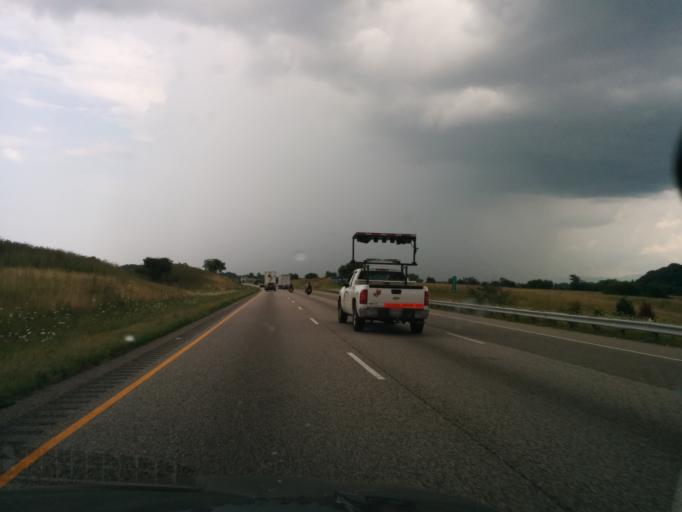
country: US
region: Virginia
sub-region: Augusta County
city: Verona
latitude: 38.1701
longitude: -79.0062
